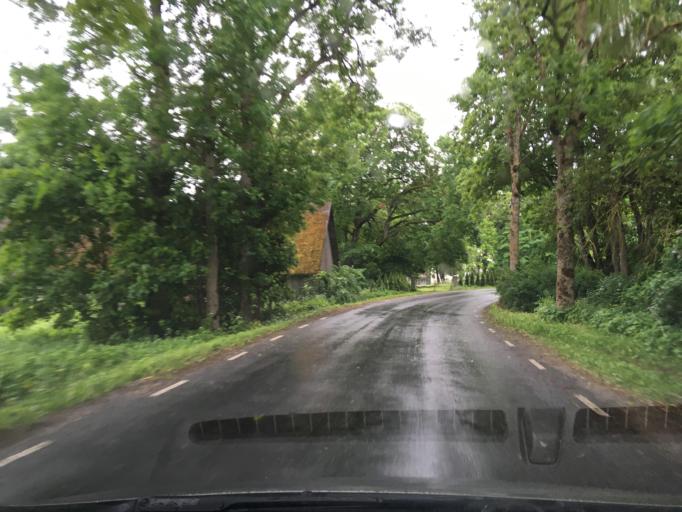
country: EE
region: Laeaene
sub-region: Lihula vald
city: Lihula
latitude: 58.6677
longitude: 23.7682
